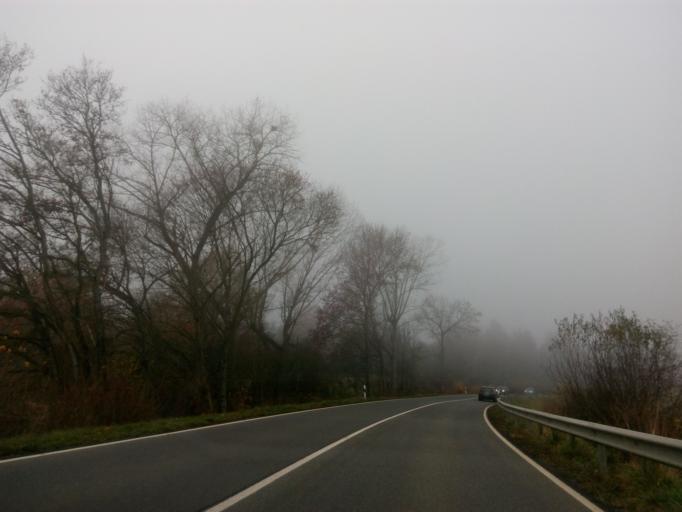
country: DE
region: Rheinland-Pfalz
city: Sien
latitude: 49.6916
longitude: 7.5096
